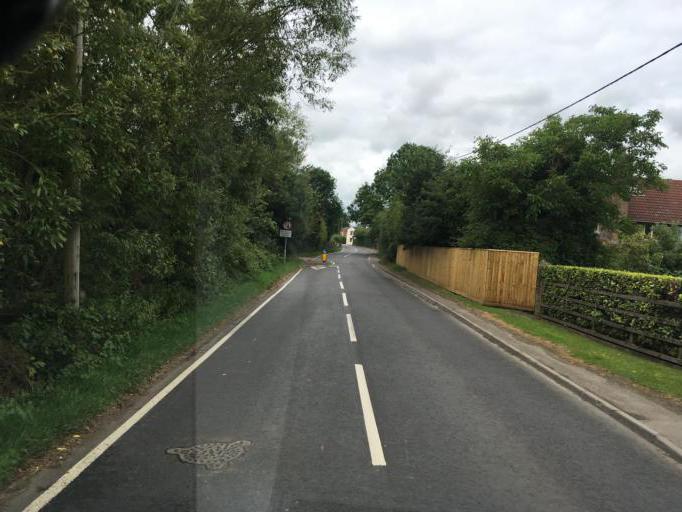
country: GB
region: England
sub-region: Gloucestershire
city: Stonehouse
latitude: 51.7407
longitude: -2.3223
